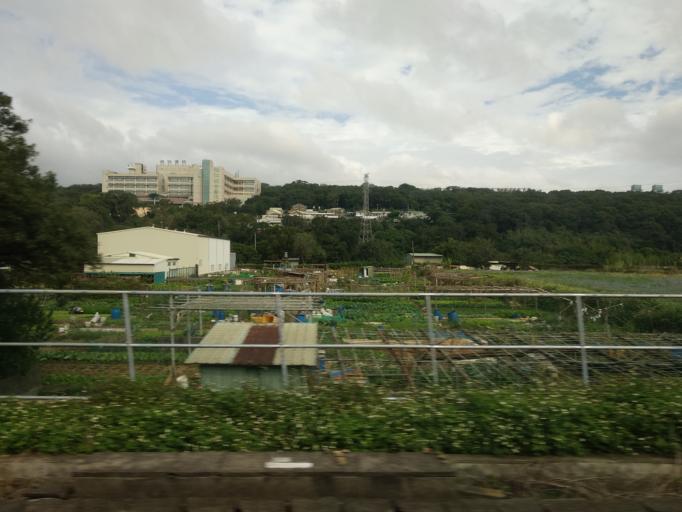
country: TW
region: Taiwan
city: Daxi
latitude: 24.9139
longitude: 121.1564
